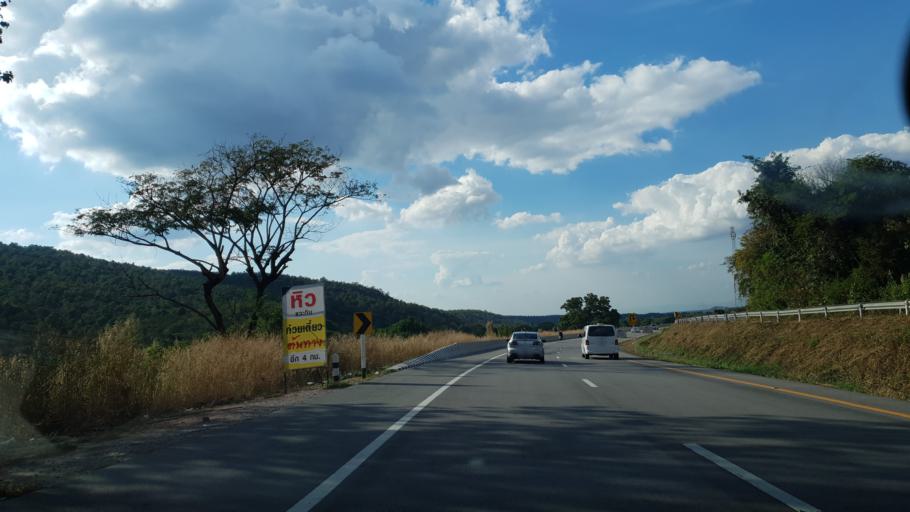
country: TH
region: Lampang
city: Mae Tha
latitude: 18.0899
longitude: 99.6494
